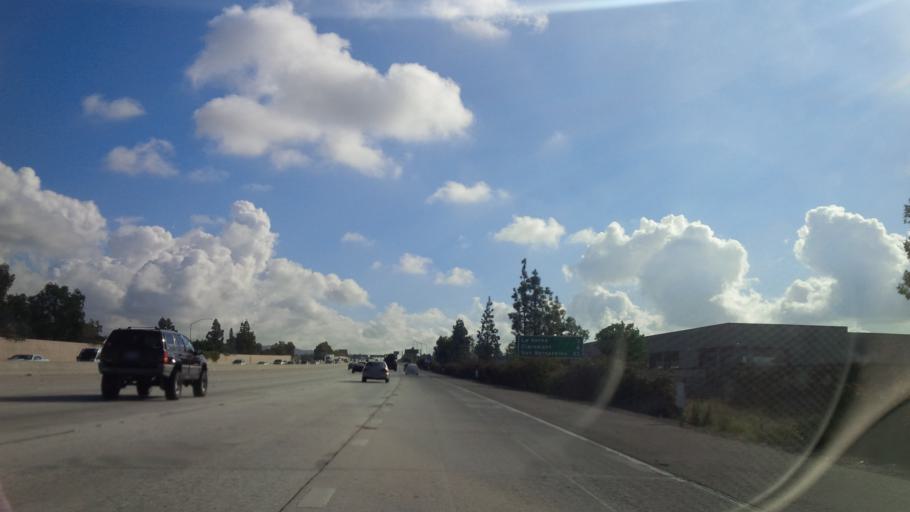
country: US
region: California
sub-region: Los Angeles County
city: San Dimas
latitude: 34.1196
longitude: -117.8145
